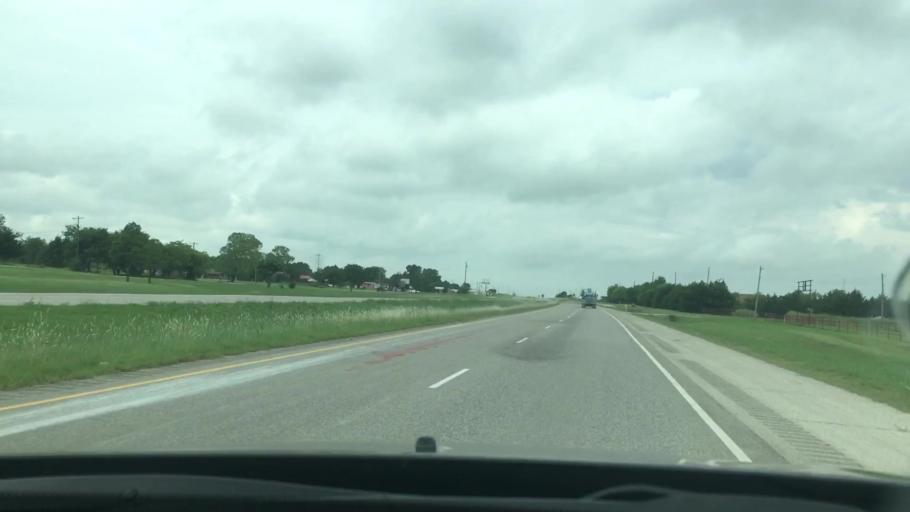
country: US
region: Oklahoma
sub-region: Carter County
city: Wilson
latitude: 34.1735
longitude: -97.4312
